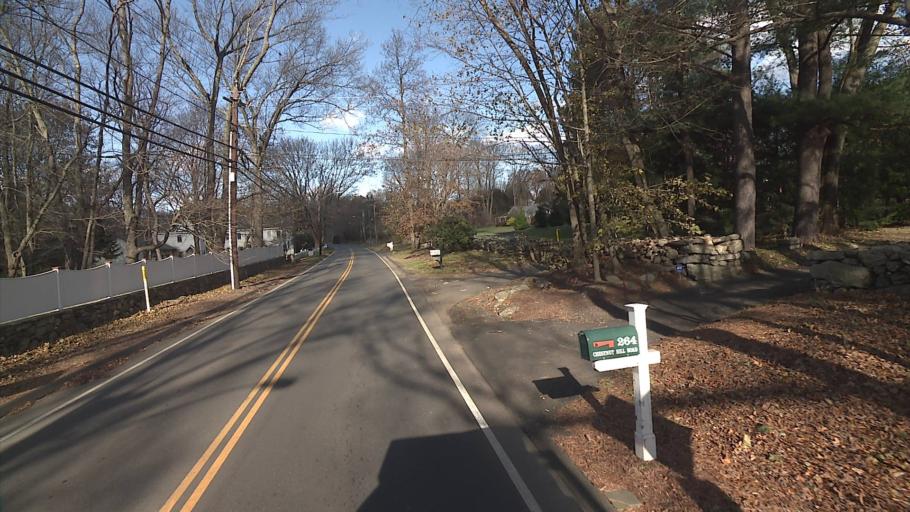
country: US
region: Connecticut
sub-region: Fairfield County
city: Westport
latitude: 41.1630
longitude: -73.3935
